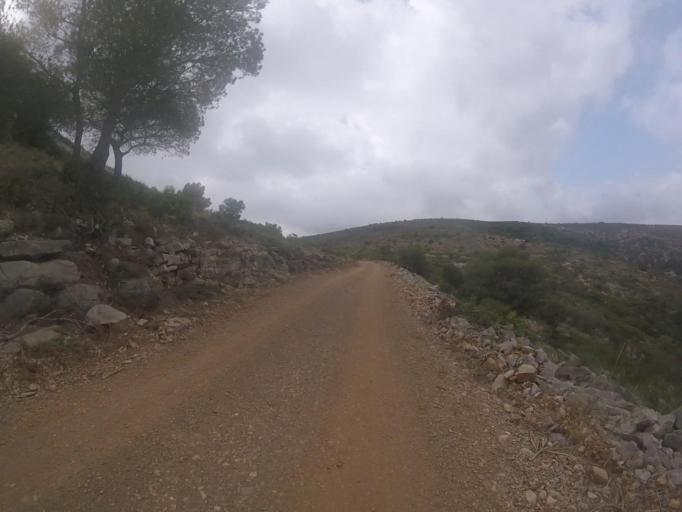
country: ES
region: Valencia
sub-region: Provincia de Castello
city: Santa Magdalena de Pulpis
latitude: 40.3456
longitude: 0.3220
